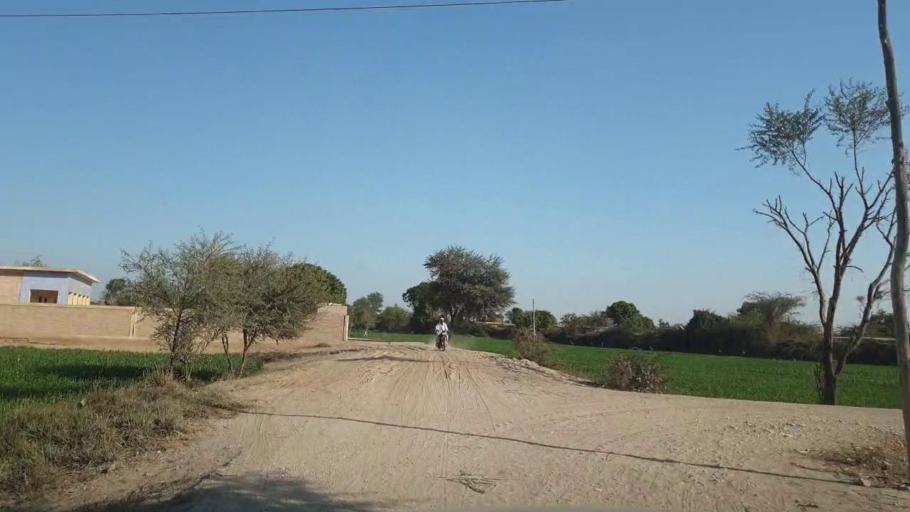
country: PK
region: Sindh
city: Tando Adam
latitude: 25.6890
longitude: 68.6894
